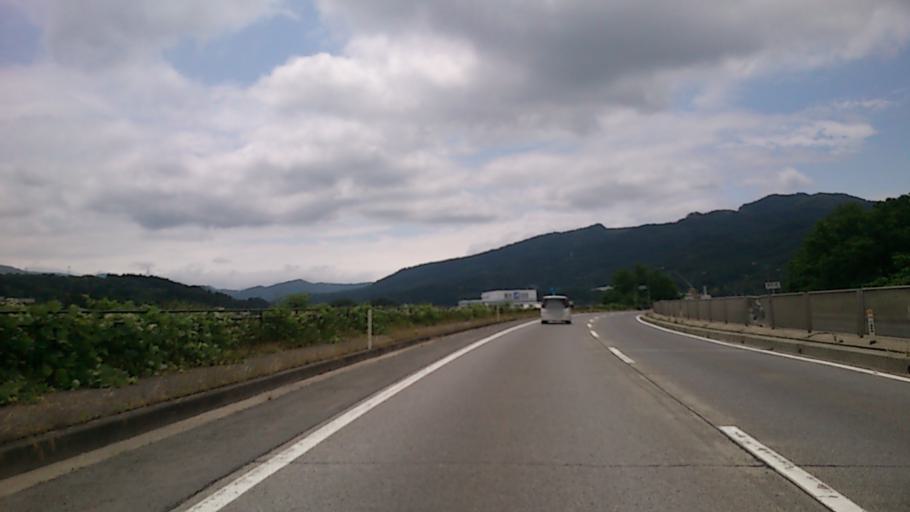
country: JP
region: Yamagata
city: Kaminoyama
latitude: 38.1705
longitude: 140.3062
